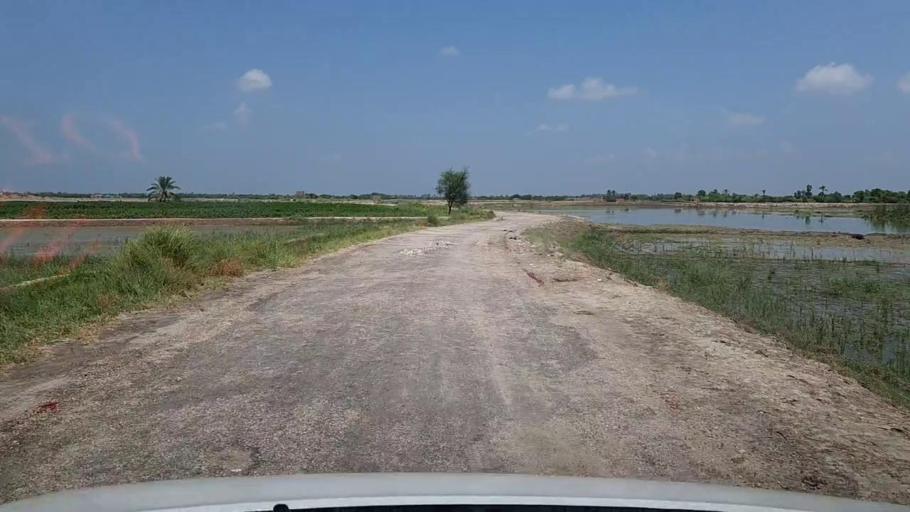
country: PK
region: Sindh
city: Kandiaro
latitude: 26.9853
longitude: 68.2192
